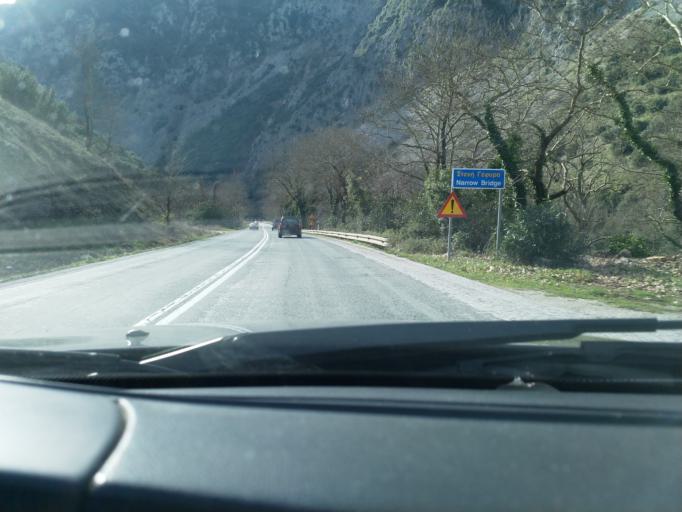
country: GR
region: Epirus
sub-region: Nomos Prevezis
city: Pappadates
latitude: 39.4026
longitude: 20.8344
